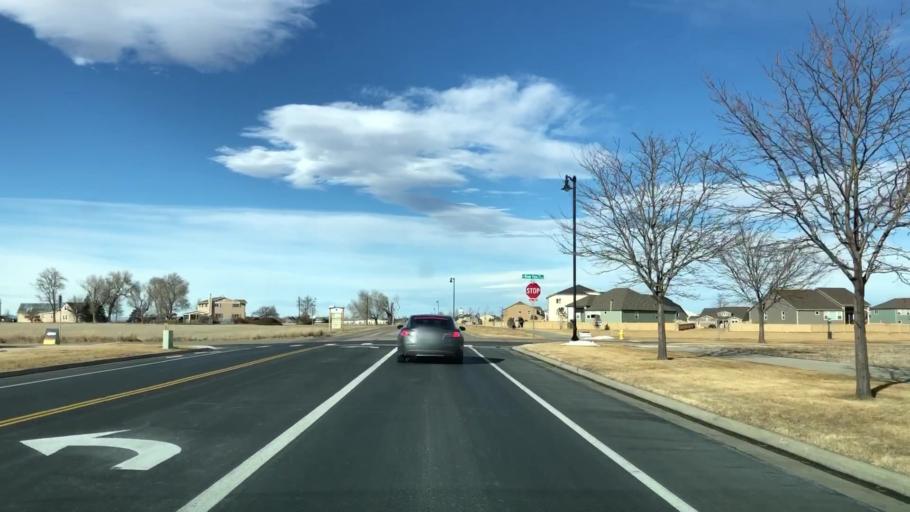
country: US
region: Colorado
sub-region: Weld County
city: Windsor
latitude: 40.5082
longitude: -104.9629
